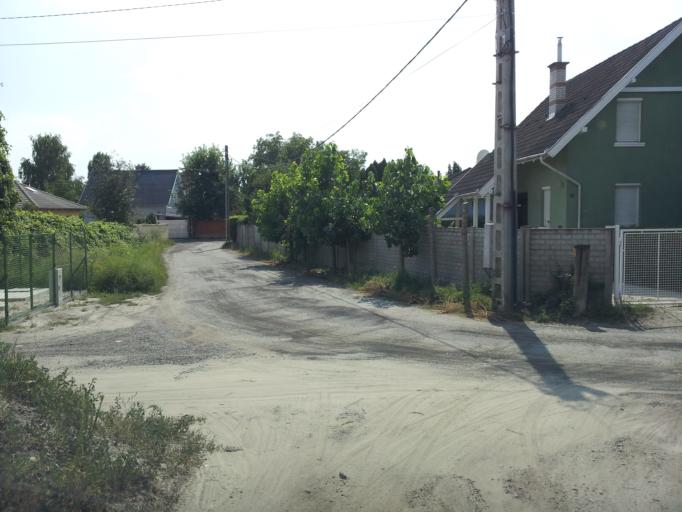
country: HU
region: Pest
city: Szigetszentmiklos
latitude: 47.3296
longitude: 19.0381
